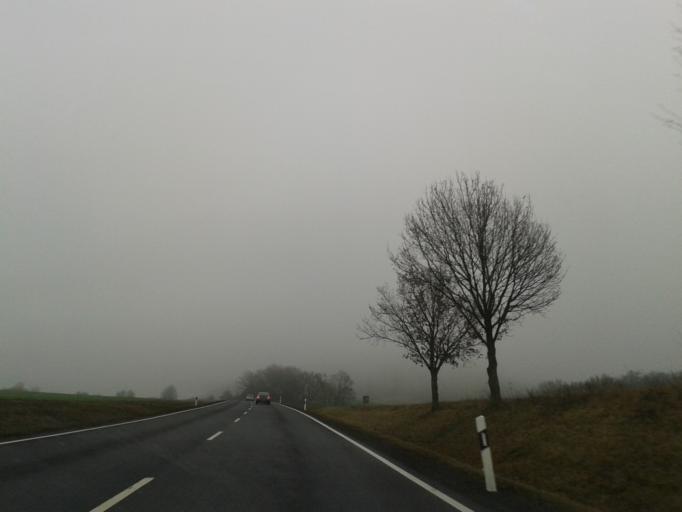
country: DE
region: Bavaria
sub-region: Regierungsbezirk Unterfranken
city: Hofheim in Unterfranken
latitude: 50.1243
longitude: 10.5592
